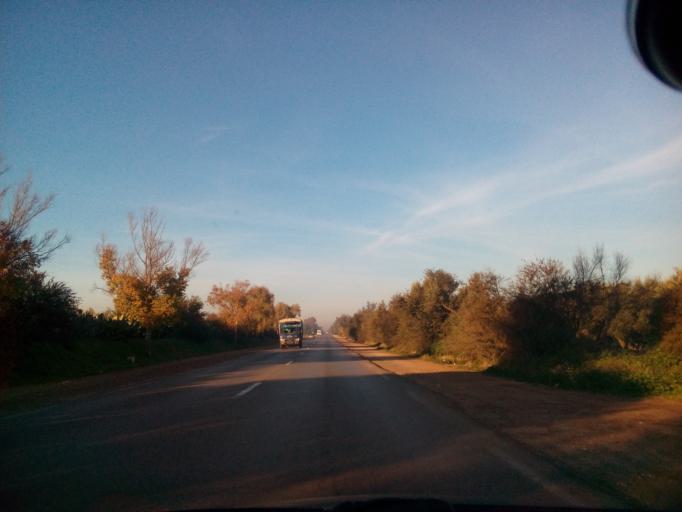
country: DZ
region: Relizane
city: Relizane
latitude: 35.7255
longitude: 0.3887
